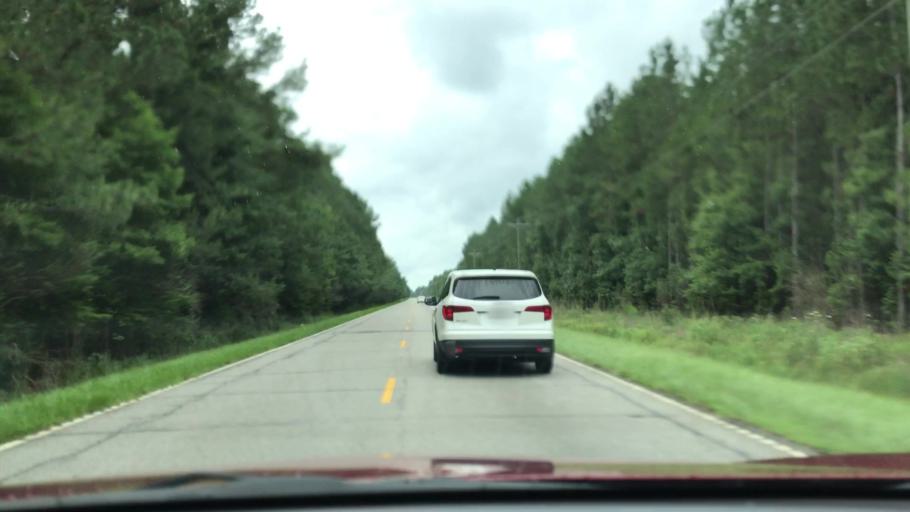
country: US
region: South Carolina
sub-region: Georgetown County
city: Murrells Inlet
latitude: 33.5852
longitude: -79.2060
